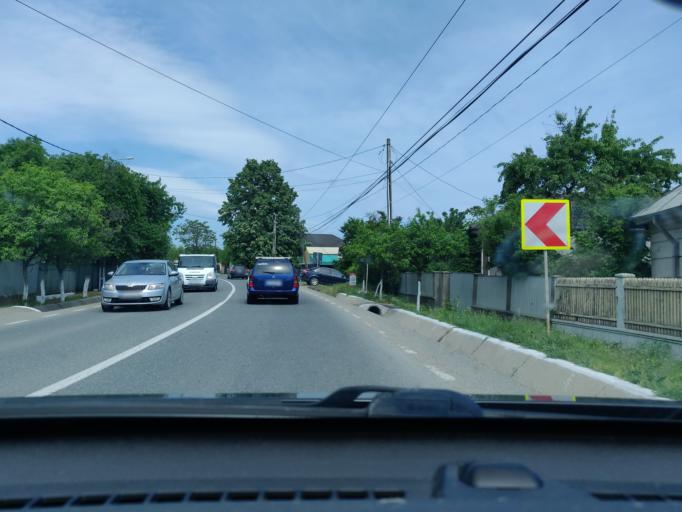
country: RO
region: Vrancea
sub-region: Comuna Bolotesti
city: Gagesti
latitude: 45.8599
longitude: 27.0495
